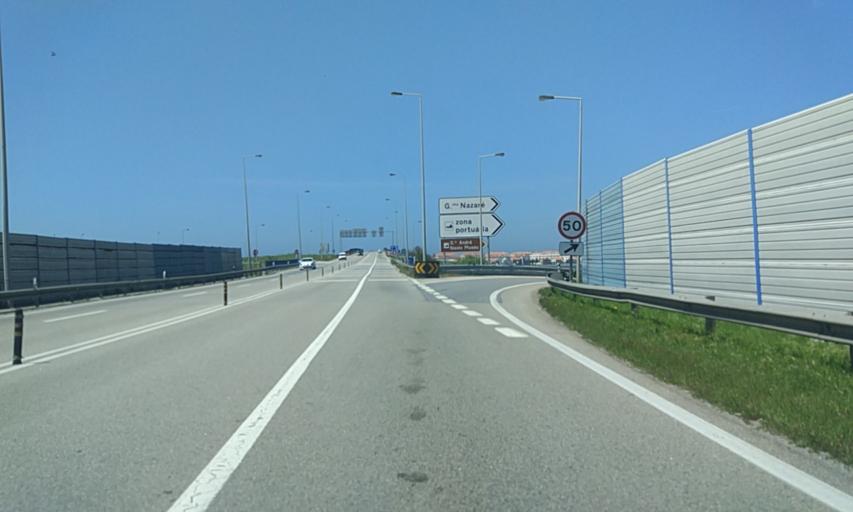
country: PT
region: Aveiro
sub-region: Ilhavo
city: Gafanha da Encarnacao
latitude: 40.6272
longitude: -8.7301
